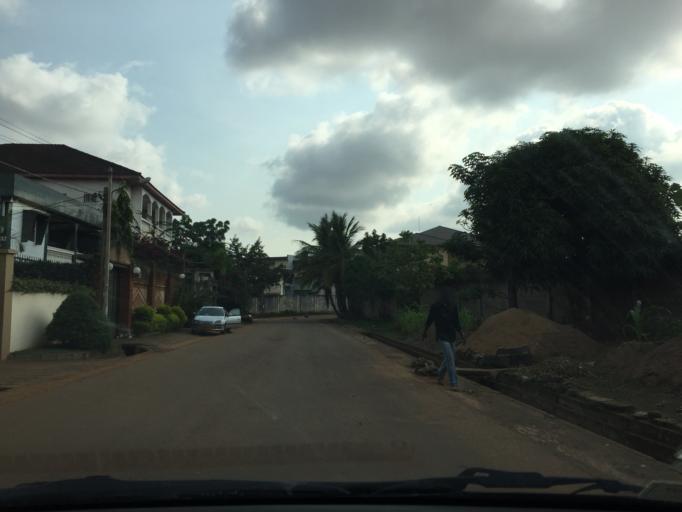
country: CM
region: Centre
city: Yaounde
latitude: 3.8835
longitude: 11.5149
